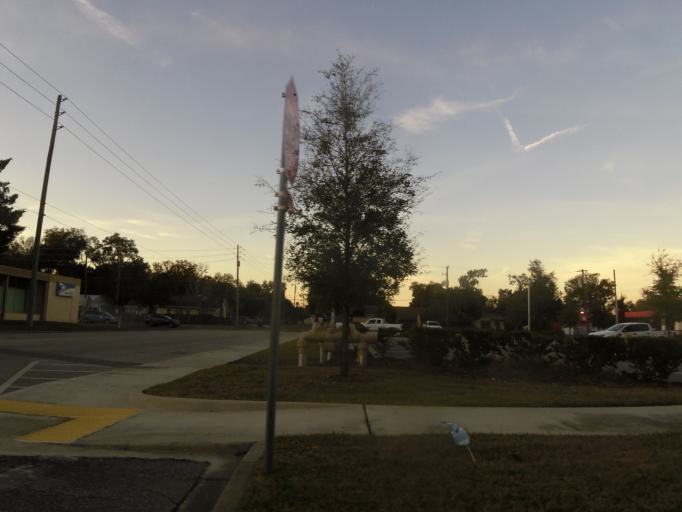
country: US
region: Florida
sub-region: Clay County
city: Green Cove Springs
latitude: 29.9940
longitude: -81.6806
